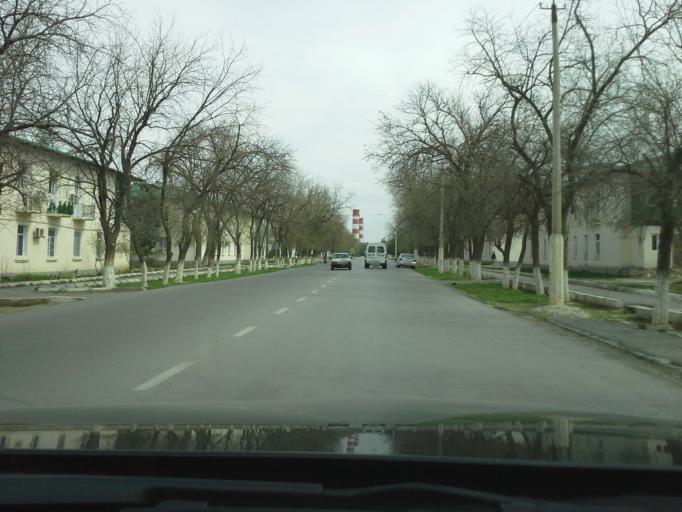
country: TM
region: Ahal
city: Abadan
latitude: 38.0606
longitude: 58.1561
